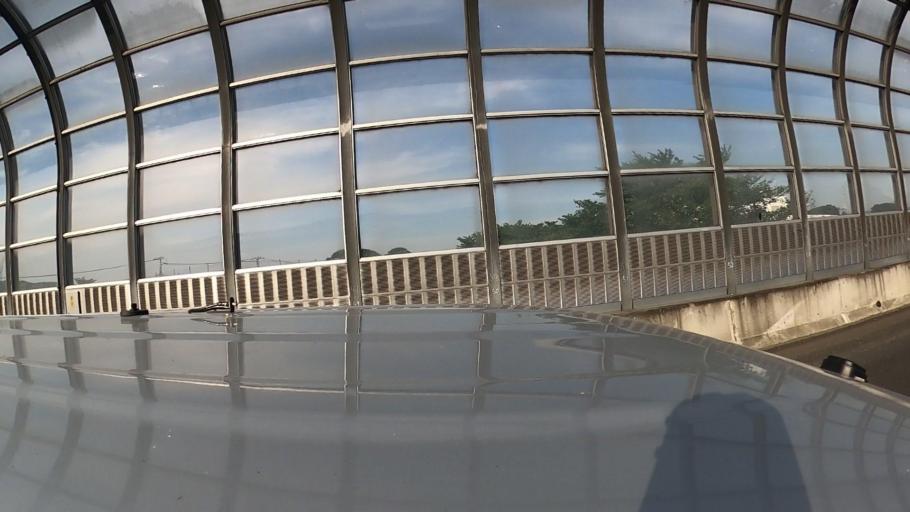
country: JP
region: Saitama
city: Asaka
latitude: 35.7760
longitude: 139.5674
